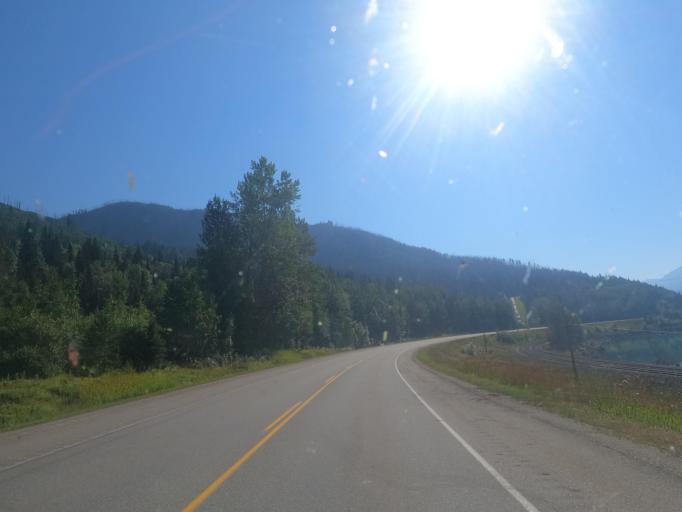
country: CA
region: Alberta
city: Jasper Park Lodge
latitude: 52.9523
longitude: -118.8686
